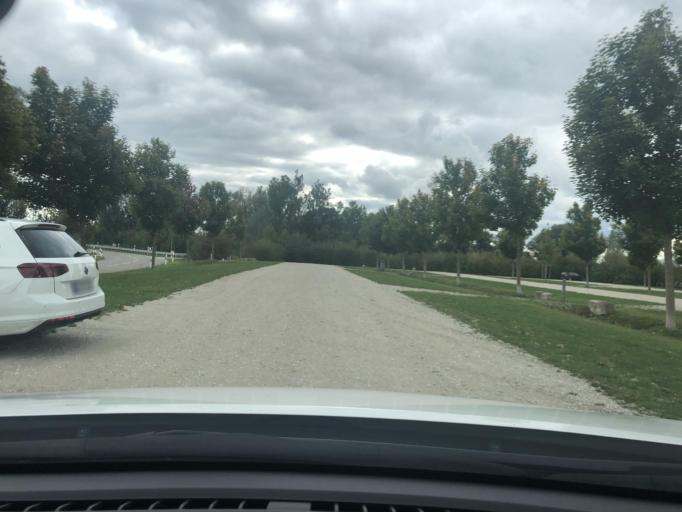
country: DE
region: Bavaria
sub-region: Upper Bavaria
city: Bergkirchen
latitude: 48.2433
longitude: 11.3375
